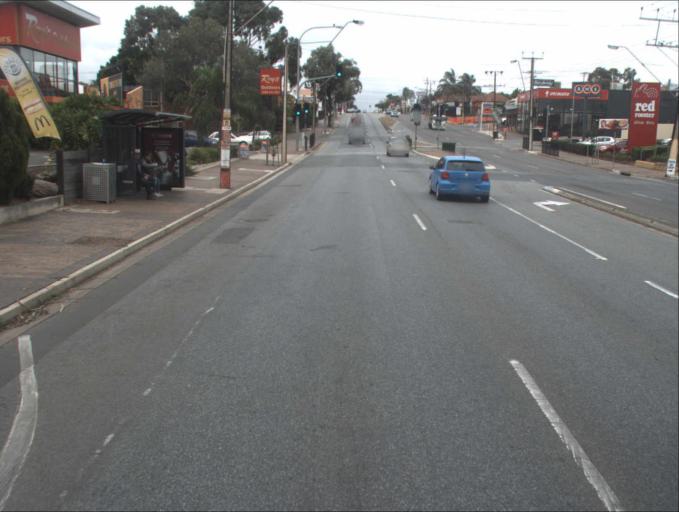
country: AU
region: South Australia
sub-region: Port Adelaide Enfield
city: Blair Athol
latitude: -34.8614
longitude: 138.6012
